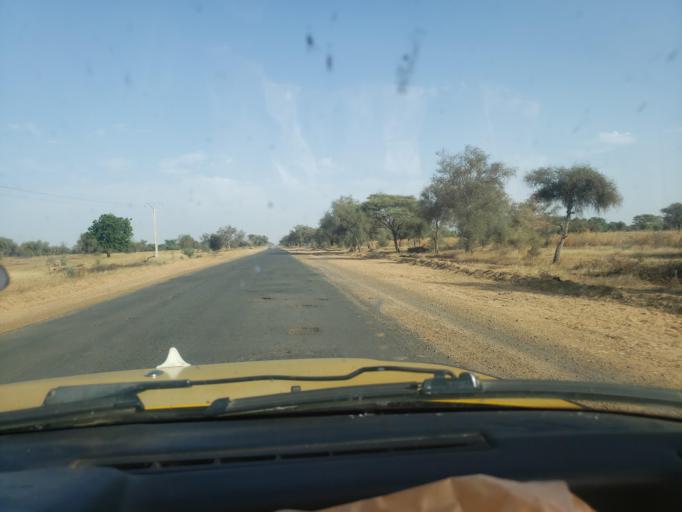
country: SN
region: Louga
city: Louga
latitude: 15.5061
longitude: -15.9626
